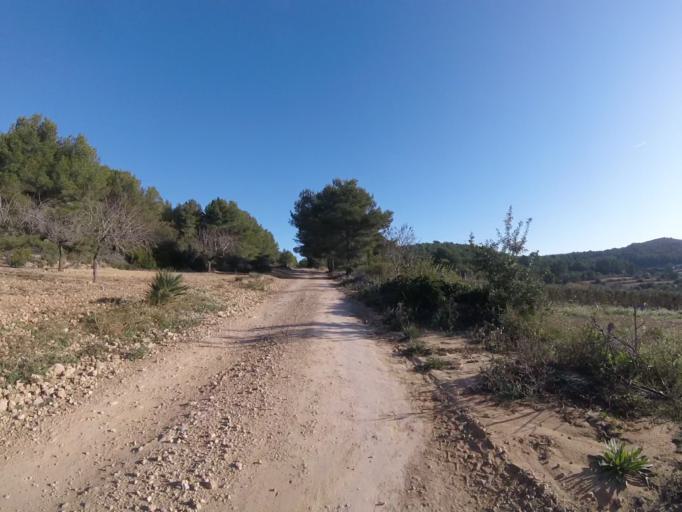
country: ES
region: Valencia
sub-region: Provincia de Castello
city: Torreblanca
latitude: 40.2521
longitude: 0.1867
